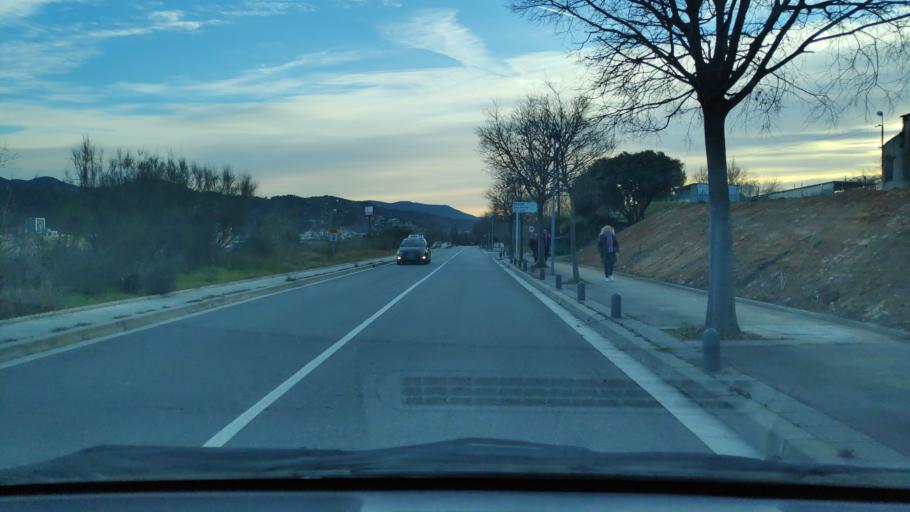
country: ES
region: Catalonia
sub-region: Provincia de Barcelona
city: Montmelo
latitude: 41.5627
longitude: 2.2577
